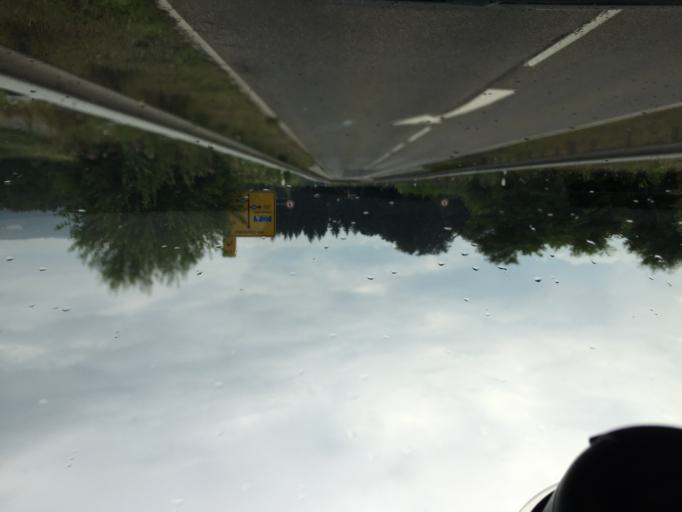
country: DE
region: Rheinland-Pfalz
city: Rengsdorf
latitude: 50.4920
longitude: 7.4962
